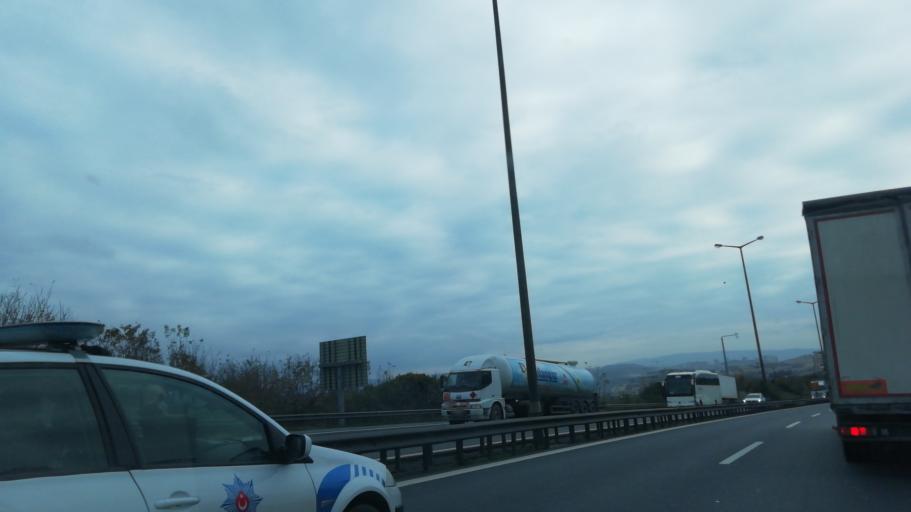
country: TR
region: Kocaeli
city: Izmit
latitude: 40.7836
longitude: 29.9333
